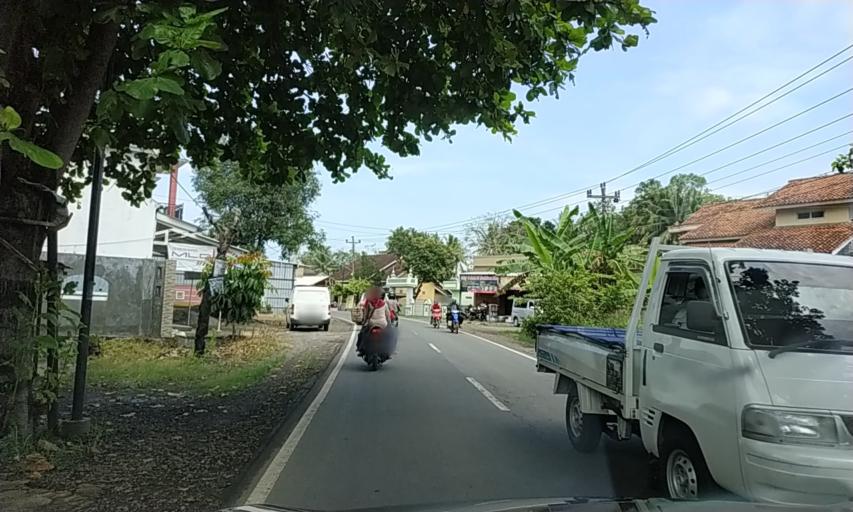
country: ID
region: Central Java
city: Sidareja
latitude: -7.4940
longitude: 108.7901
